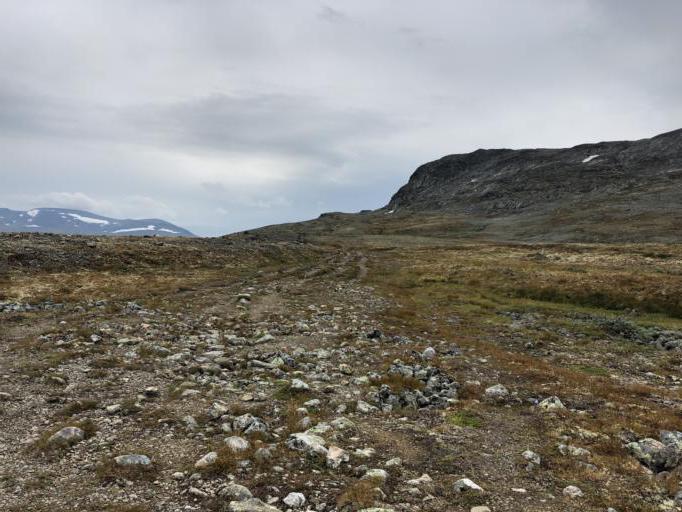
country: NO
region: Oppland
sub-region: Lom
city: Fossbergom
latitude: 61.5213
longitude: 8.8105
